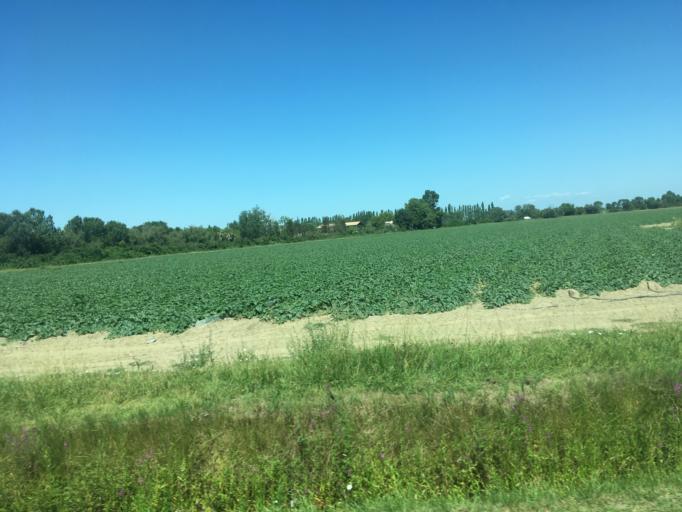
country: FR
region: Languedoc-Roussillon
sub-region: Departement du Gard
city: Saint-Gilles
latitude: 43.5824
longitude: 4.4645
